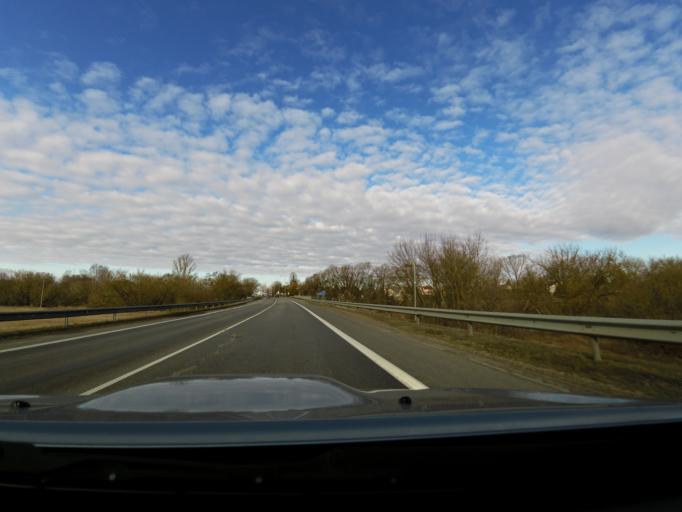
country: LT
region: Panevezys
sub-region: Panevezys City
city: Panevezys
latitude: 55.7350
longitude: 24.2374
